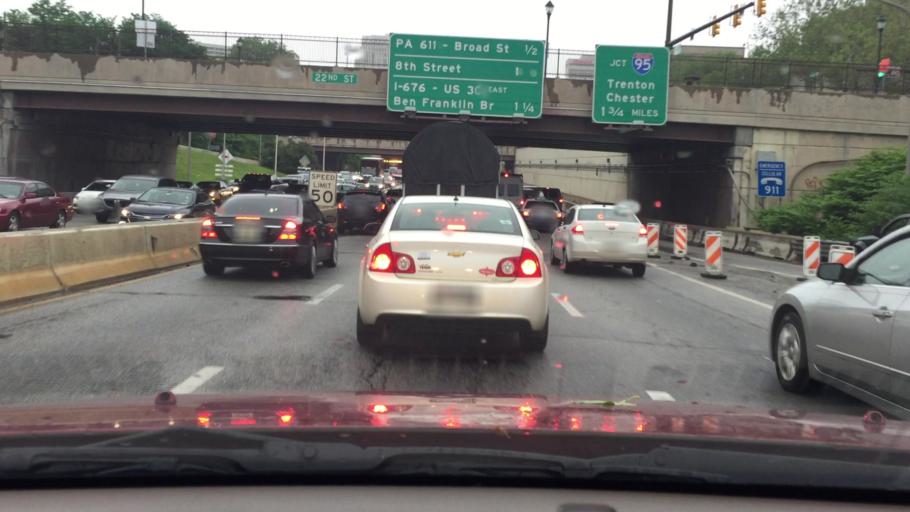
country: US
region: Pennsylvania
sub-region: Philadelphia County
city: Philadelphia
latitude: 39.9596
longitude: -75.1762
